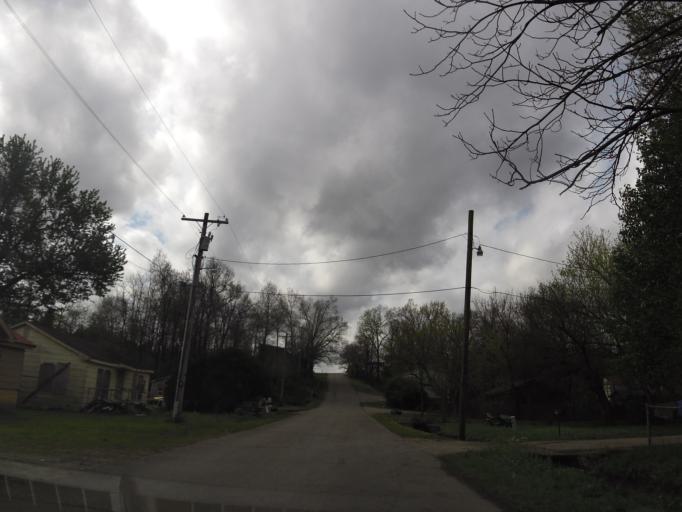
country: US
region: Missouri
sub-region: Butler County
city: Poplar Bluff
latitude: 36.7534
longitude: -90.4003
